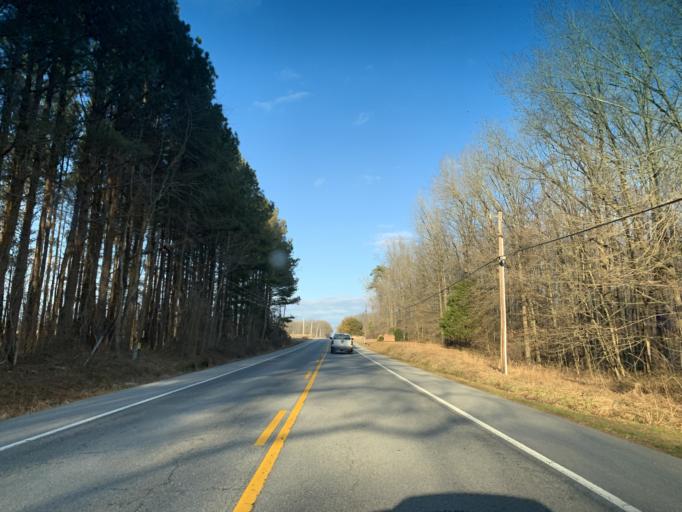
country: US
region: Maryland
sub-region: Queen Anne's County
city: Kingstown
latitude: 39.1554
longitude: -75.9560
